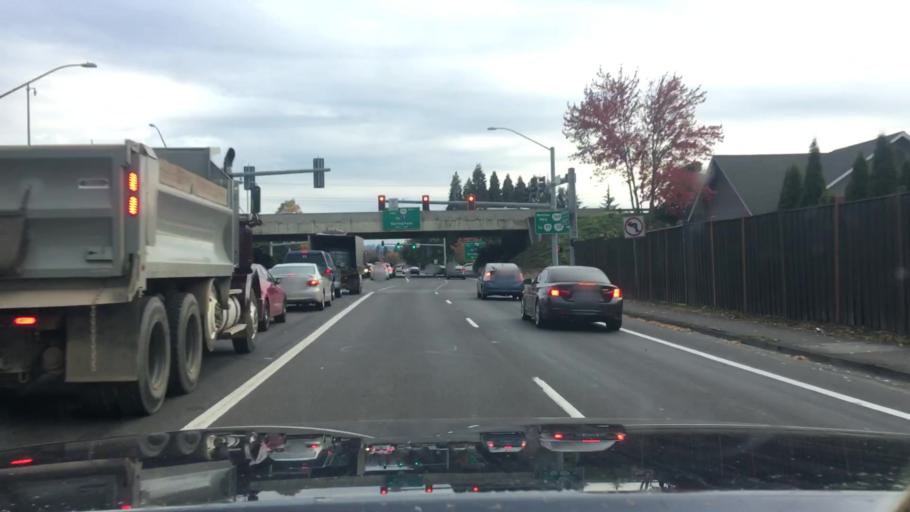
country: US
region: Oregon
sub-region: Lane County
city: Eugene
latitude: 44.0886
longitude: -123.0677
